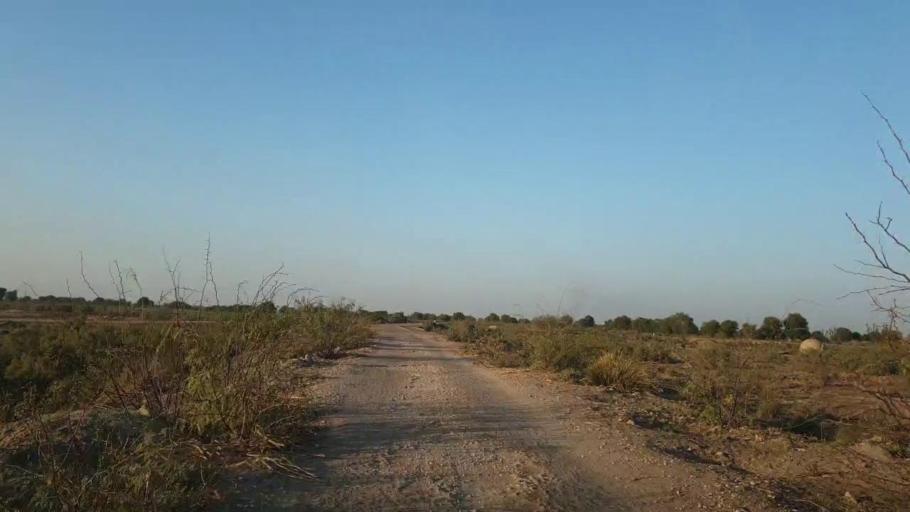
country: PK
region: Sindh
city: Mirpur Khas
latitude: 25.6860
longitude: 69.0504
